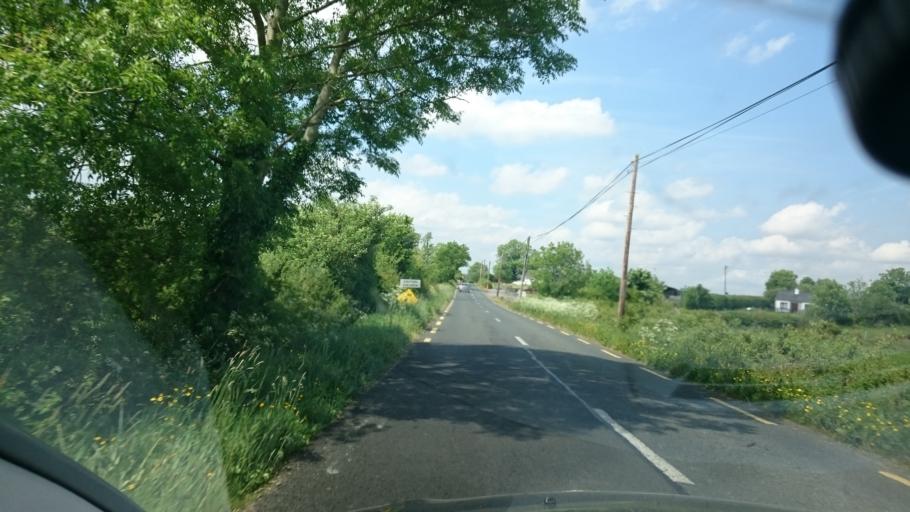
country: IE
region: Connaught
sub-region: Sligo
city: Tobercurry
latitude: 54.0563
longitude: -8.7949
